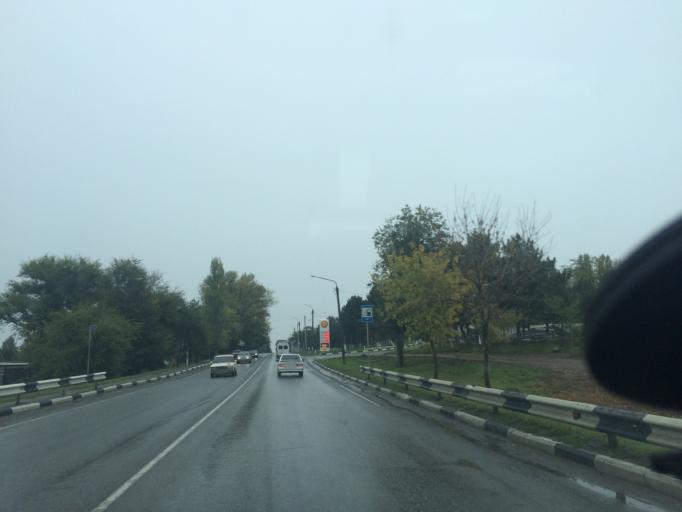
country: RU
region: Rostov
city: Azov
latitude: 47.0894
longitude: 39.4578
